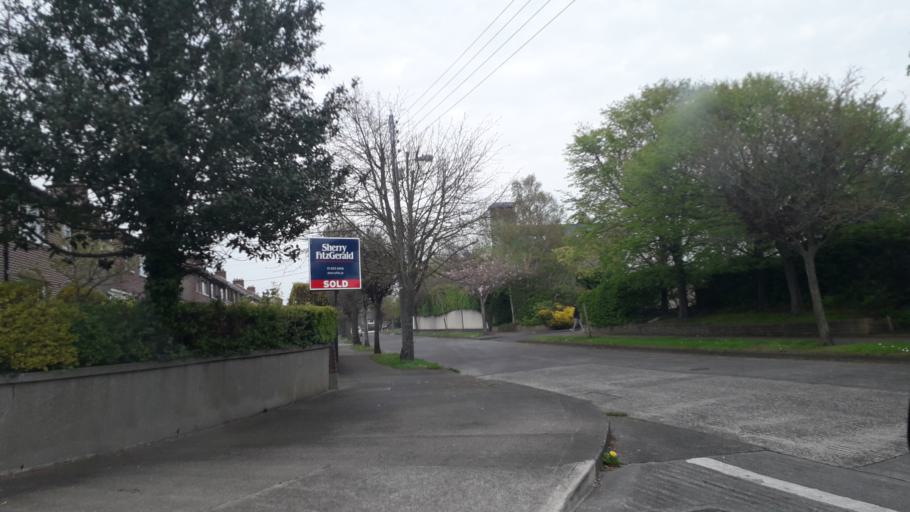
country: IE
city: Donnycarney
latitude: 53.3642
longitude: -6.2085
